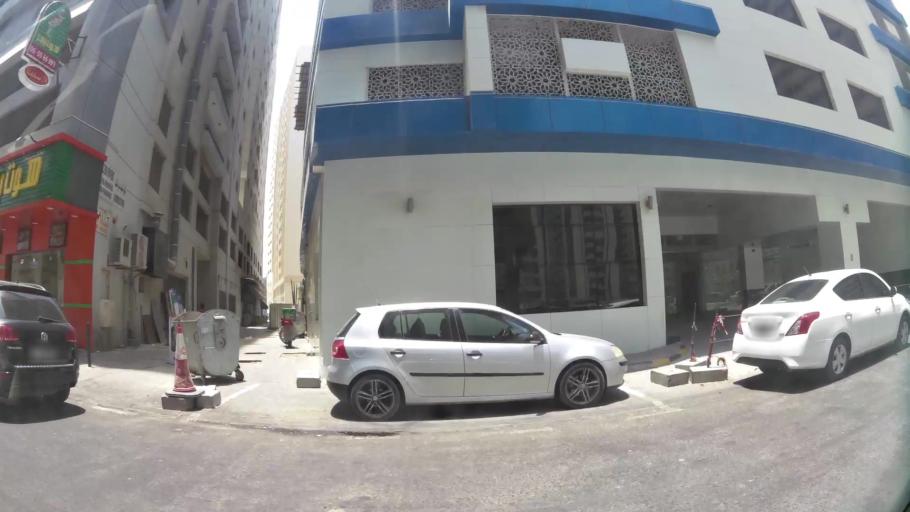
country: AE
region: Ash Shariqah
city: Sharjah
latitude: 25.3293
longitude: 55.3747
